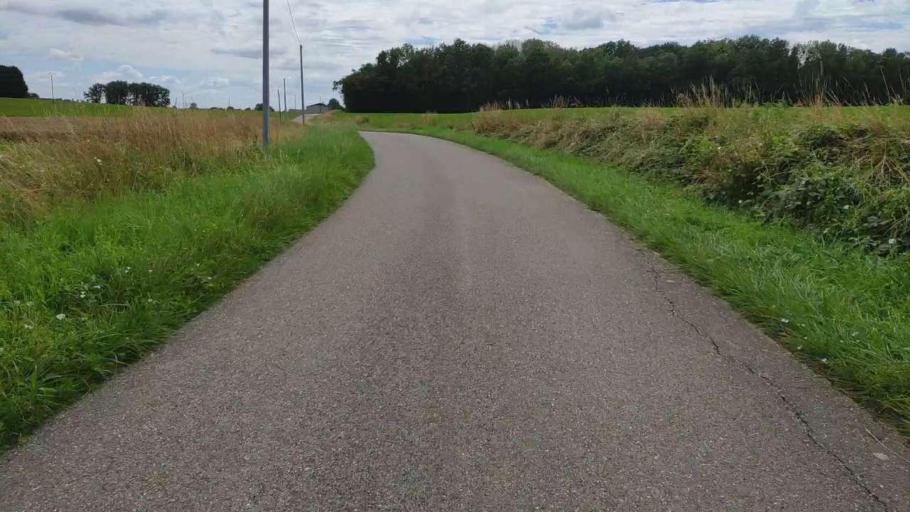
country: FR
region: Franche-Comte
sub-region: Departement du Jura
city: Chaussin
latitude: 46.8848
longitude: 5.4434
